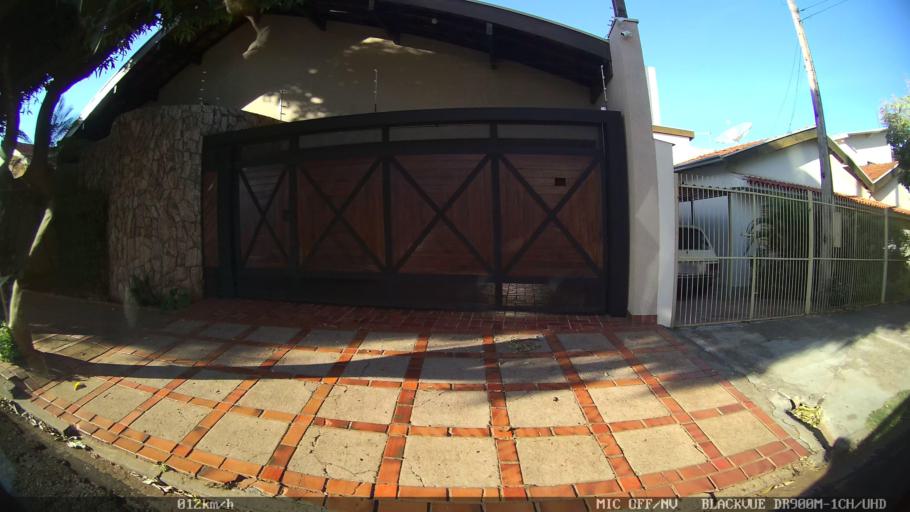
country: BR
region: Sao Paulo
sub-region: Sao Jose Do Rio Preto
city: Sao Jose do Rio Preto
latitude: -20.8270
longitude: -49.3722
